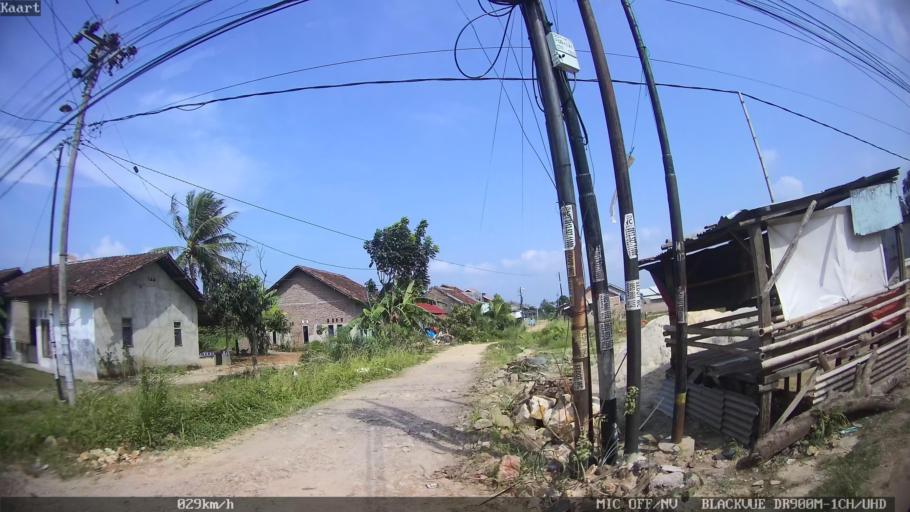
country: ID
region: Lampung
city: Kedaton
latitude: -5.3473
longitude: 105.2667
